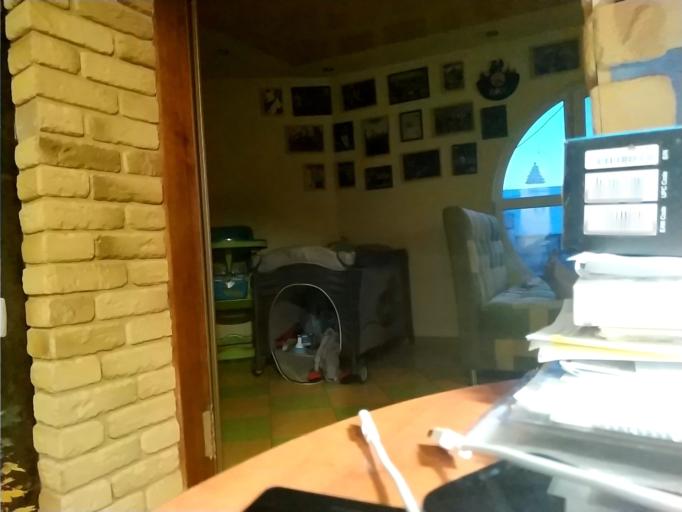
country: RU
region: Republic of Karelia
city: Belomorsk
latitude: 64.4363
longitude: 34.6571
